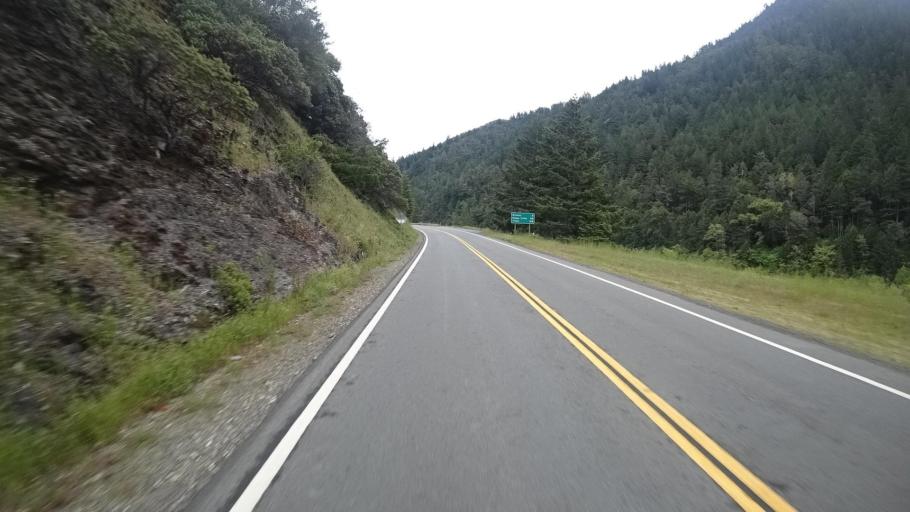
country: US
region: California
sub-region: Humboldt County
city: Willow Creek
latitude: 41.2508
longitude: -123.6418
